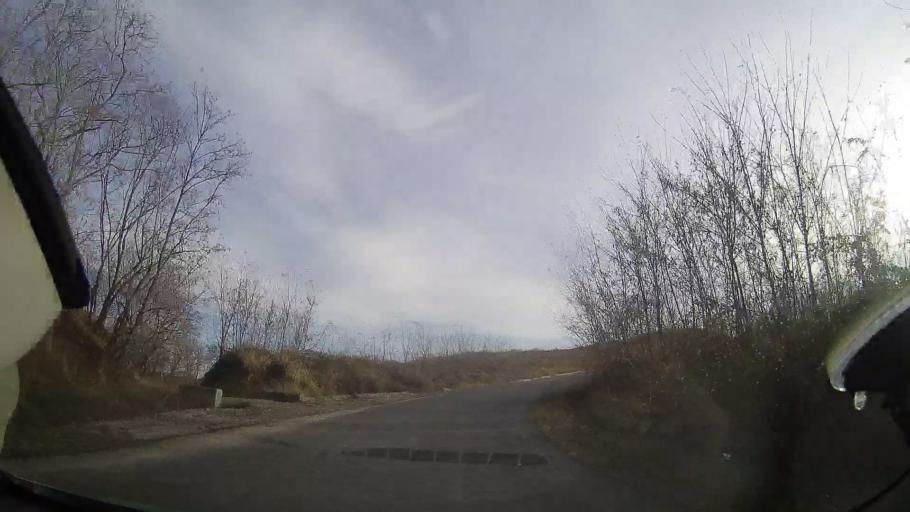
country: RO
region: Bihor
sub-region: Comuna Sarbi
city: Burzuc
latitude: 47.1313
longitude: 22.1869
